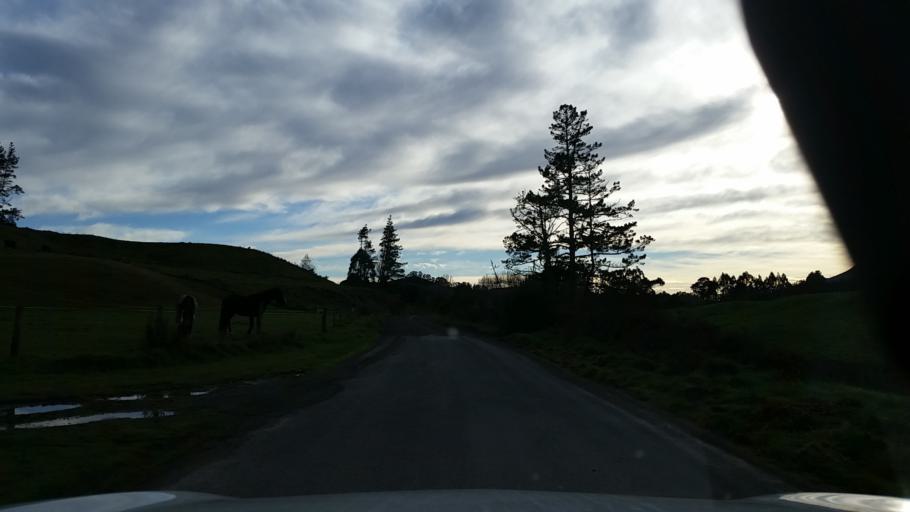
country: NZ
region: Bay of Plenty
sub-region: Rotorua District
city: Rotorua
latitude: -38.2650
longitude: 176.1586
